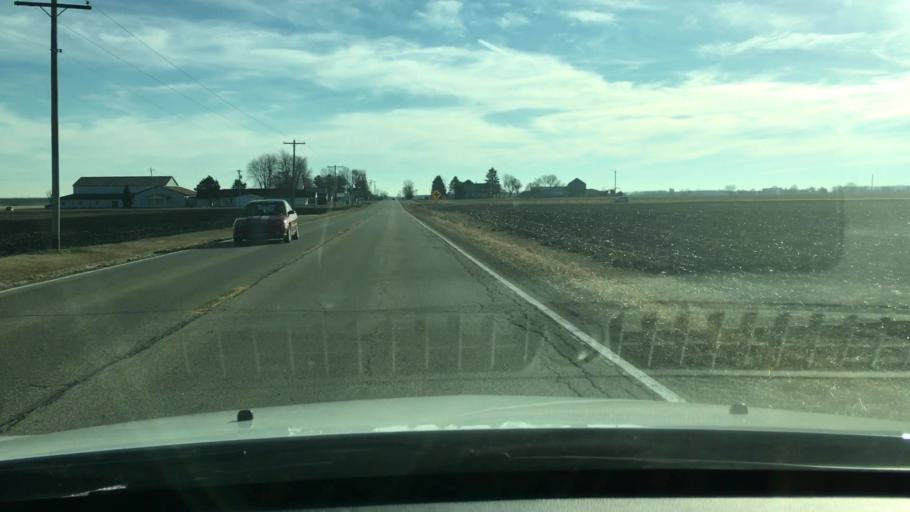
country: US
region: Illinois
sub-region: LaSalle County
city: Peru
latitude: 41.3988
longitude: -89.1260
